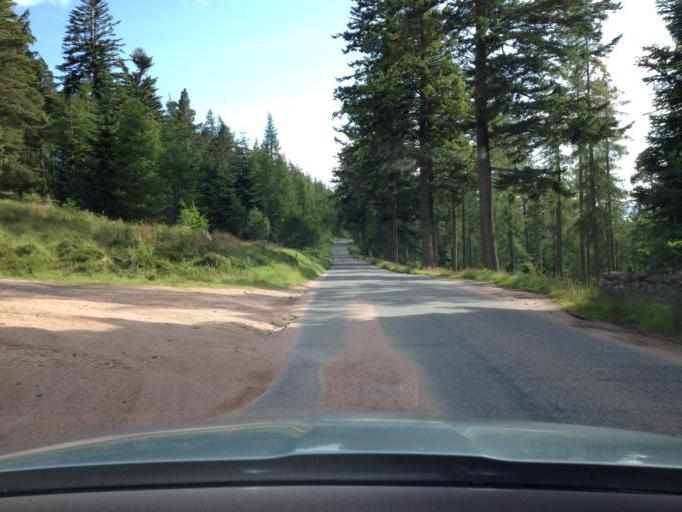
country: GB
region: Scotland
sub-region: Aberdeenshire
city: Banchory
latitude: 56.9578
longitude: -2.5809
